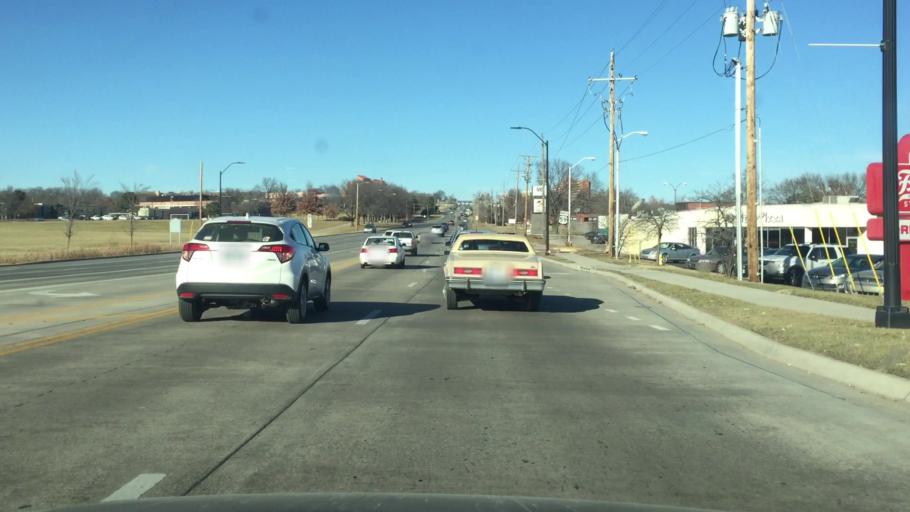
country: US
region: Kansas
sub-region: Douglas County
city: Lawrence
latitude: 38.9431
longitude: -95.2604
